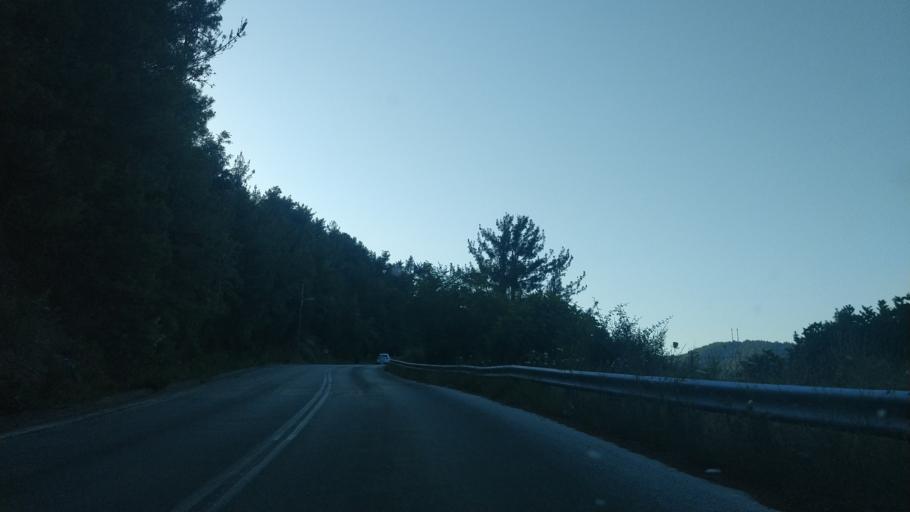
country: GR
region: East Macedonia and Thrace
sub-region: Nomos Kavalas
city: Potamia
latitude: 40.7271
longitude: 24.7333
